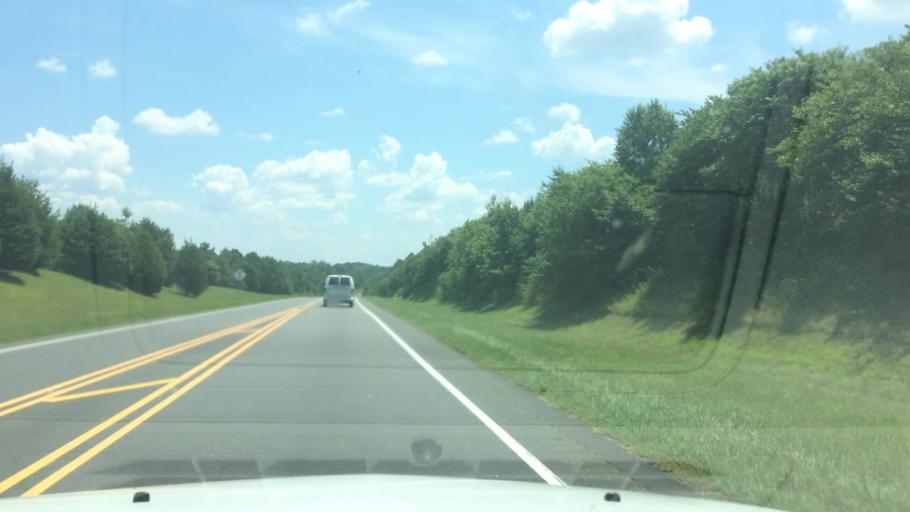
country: US
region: North Carolina
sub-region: Alexander County
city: Stony Point
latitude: 35.8506
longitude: -81.0374
